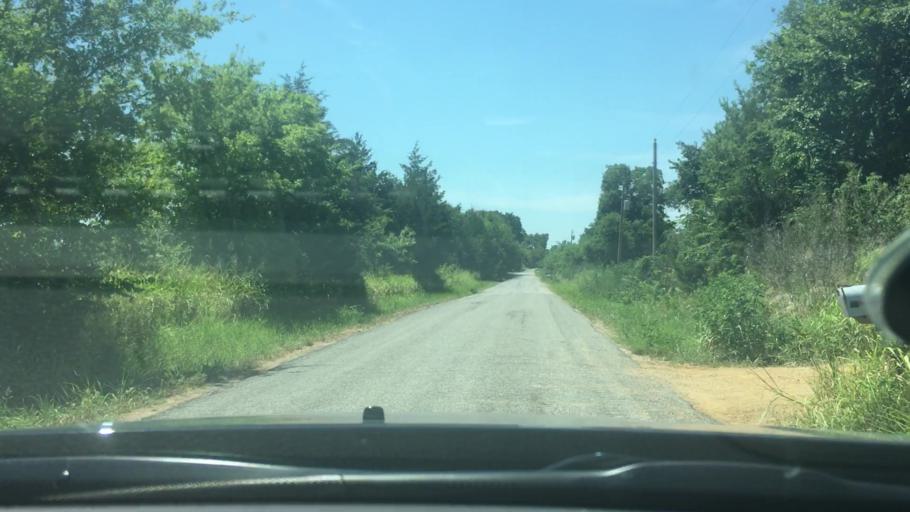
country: US
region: Oklahoma
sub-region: Bryan County
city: Durant
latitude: 33.9962
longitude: -96.2684
